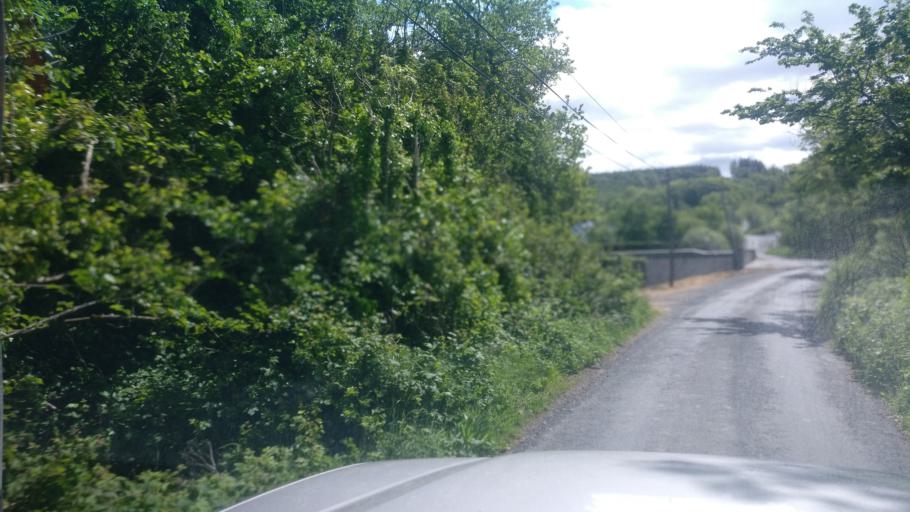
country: IE
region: Connaught
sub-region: County Galway
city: Gort
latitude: 53.1345
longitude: -8.7119
